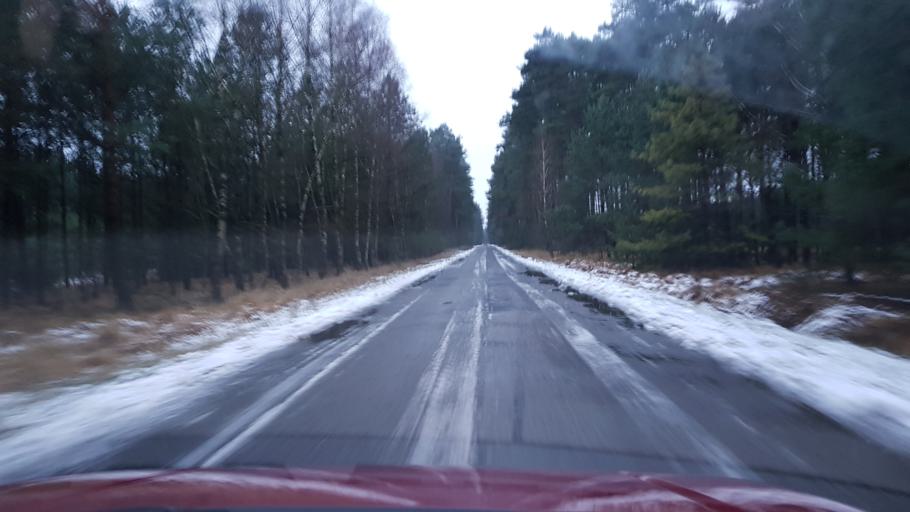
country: PL
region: West Pomeranian Voivodeship
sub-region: Powiat goleniowski
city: Goleniow
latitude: 53.4819
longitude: 14.8469
